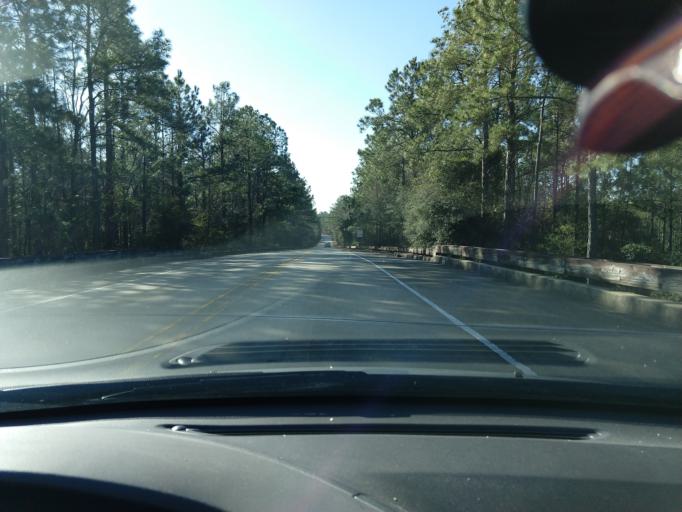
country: US
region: Mississippi
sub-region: Jackson County
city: Gulf Park Estates
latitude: 30.4094
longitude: -88.7792
